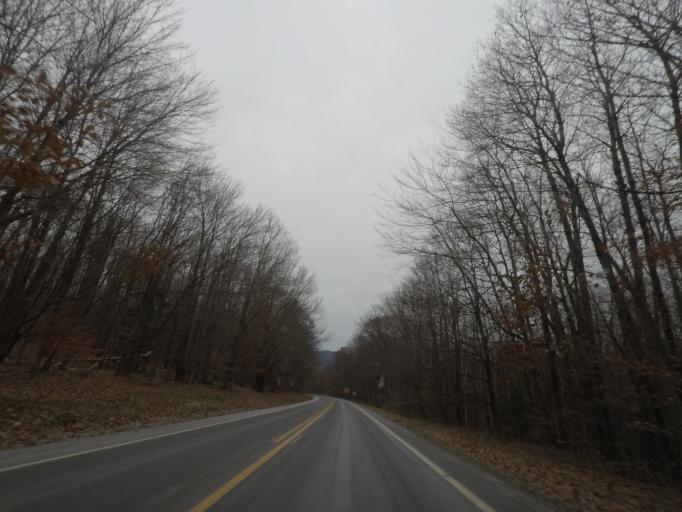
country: US
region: Massachusetts
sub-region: Berkshire County
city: Williamstown
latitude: 42.6949
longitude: -73.2387
